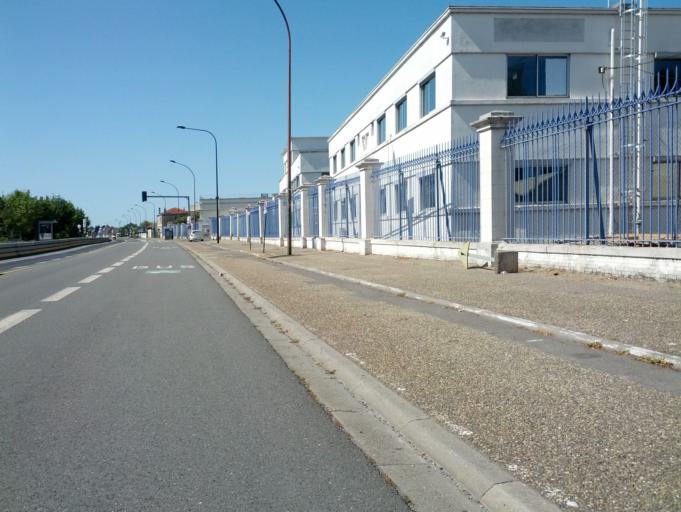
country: FR
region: Aquitaine
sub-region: Departement de la Gironde
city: Begles
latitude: 44.8264
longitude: -0.5371
